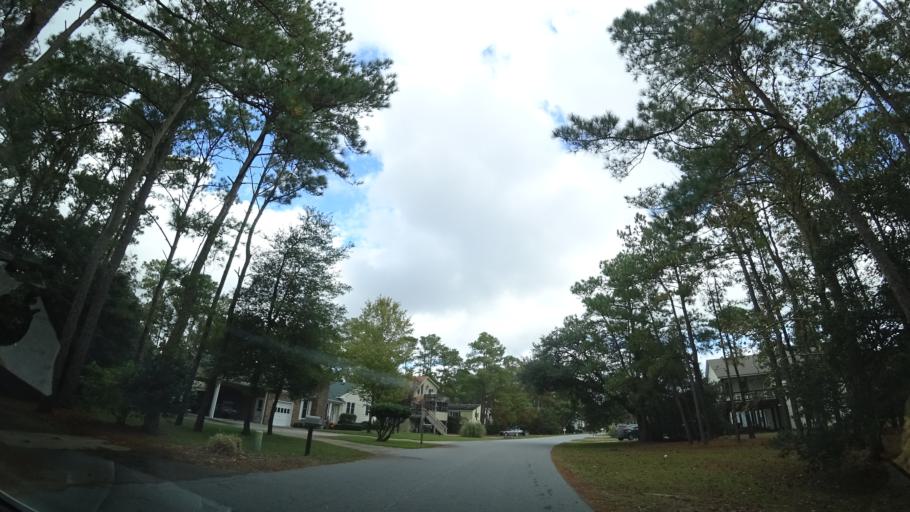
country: US
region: North Carolina
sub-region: Dare County
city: Kill Devil Hills
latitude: 35.9928
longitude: -75.6592
